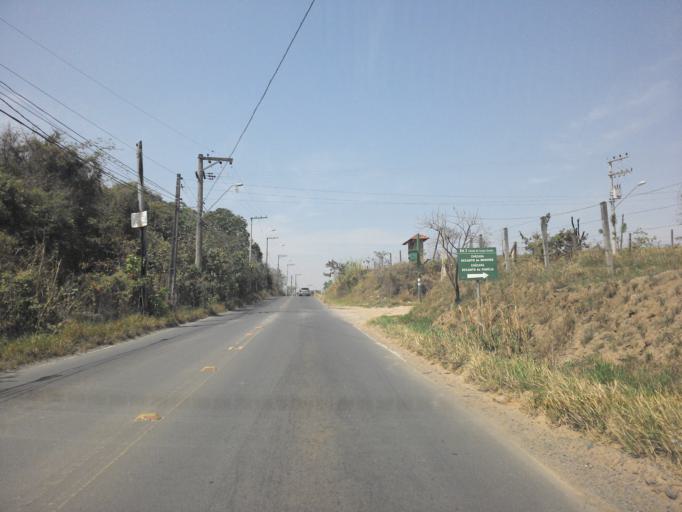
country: BR
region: Sao Paulo
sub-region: Hortolandia
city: Hortolandia
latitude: -22.9172
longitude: -47.1932
